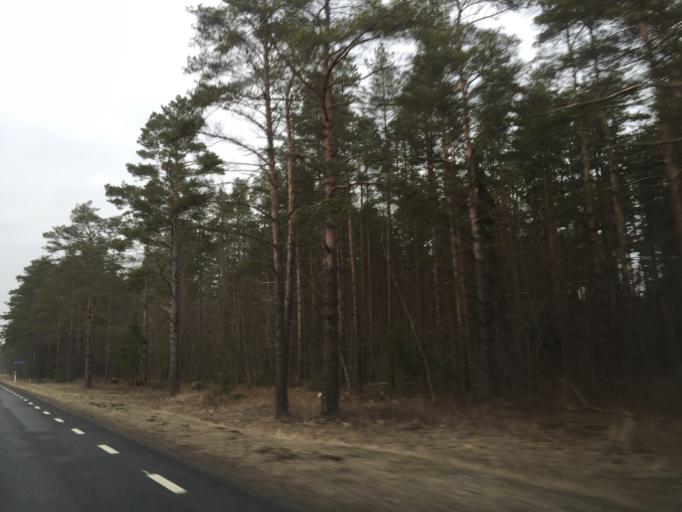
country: EE
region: Saare
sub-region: Orissaare vald
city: Orissaare
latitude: 58.5951
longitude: 23.3277
